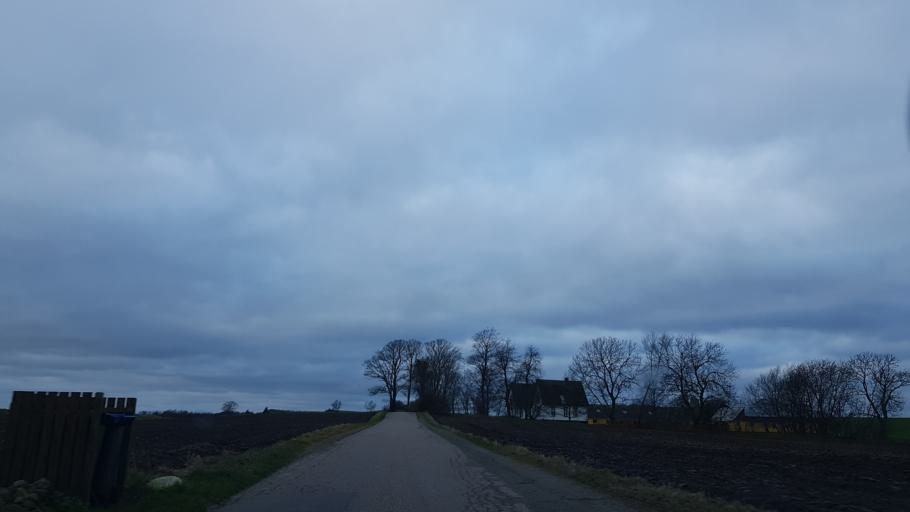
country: DK
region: Zealand
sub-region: Odsherred Kommune
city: Hojby
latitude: 55.9351
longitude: 11.5767
